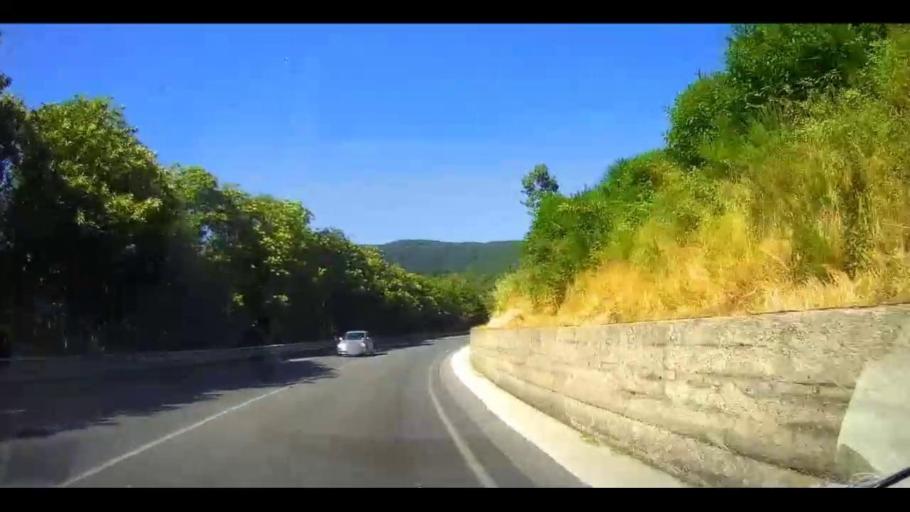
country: IT
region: Calabria
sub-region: Provincia di Cosenza
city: Celico
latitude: 39.3120
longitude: 16.3550
